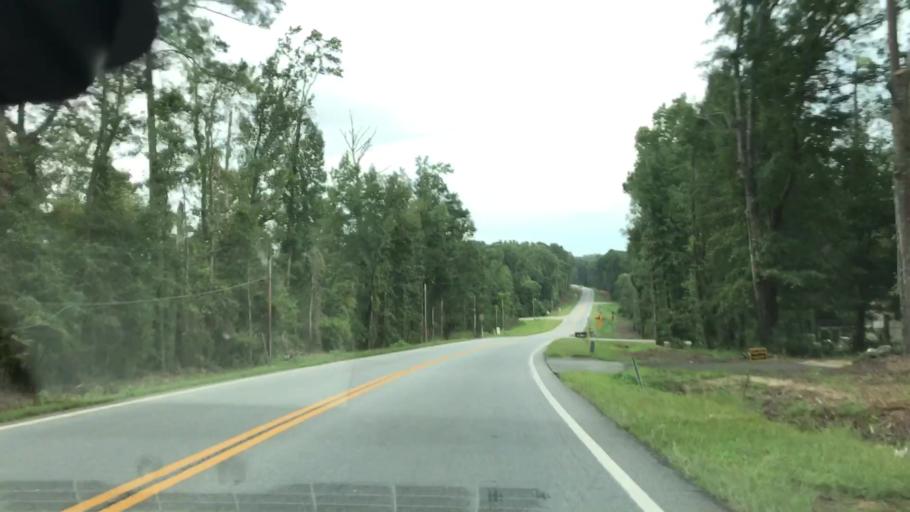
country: US
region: Georgia
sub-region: Quitman County
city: Georgetown
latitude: 31.8787
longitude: -85.0833
